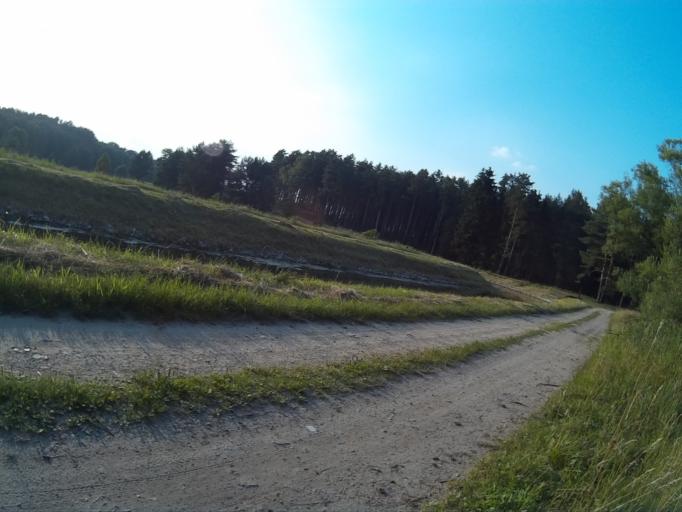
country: PL
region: Pomeranian Voivodeship
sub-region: Powiat chojnicki
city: Czersk
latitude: 53.7025
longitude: 17.9696
